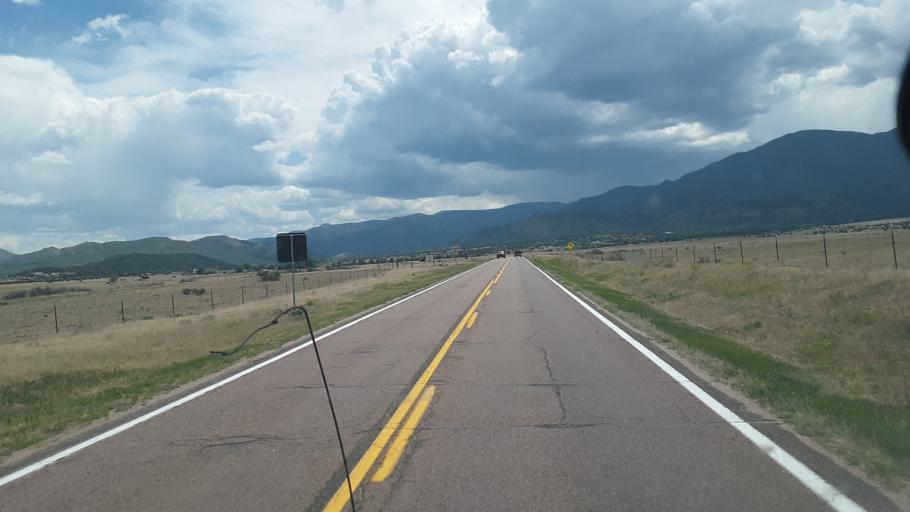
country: US
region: Colorado
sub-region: Fremont County
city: Florence
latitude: 38.2588
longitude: -105.0887
